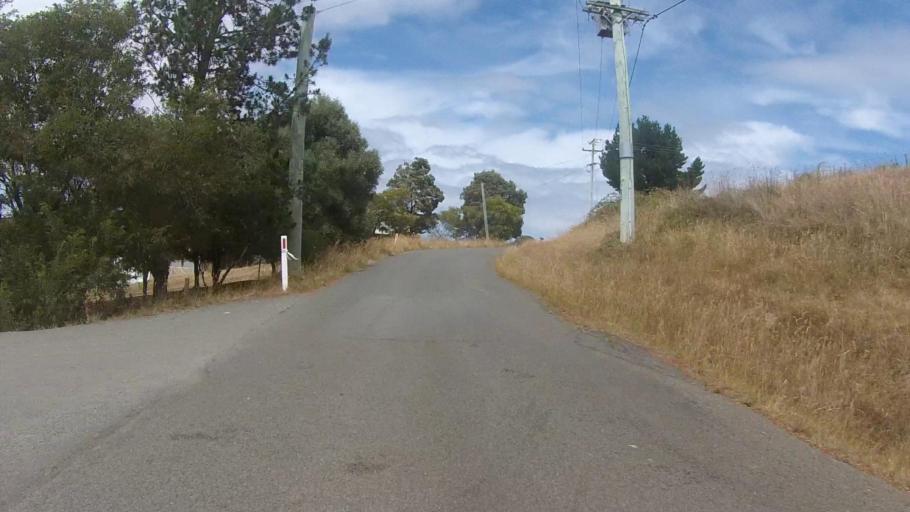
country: AU
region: Tasmania
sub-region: Kingborough
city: Blackmans Bay
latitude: -43.0566
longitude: 147.3270
